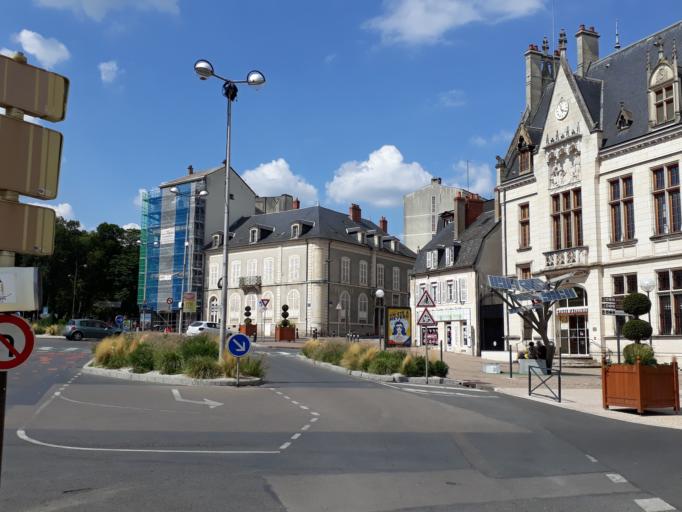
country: FR
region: Bourgogne
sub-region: Departement de la Nievre
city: Nevers
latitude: 46.9885
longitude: 3.1575
